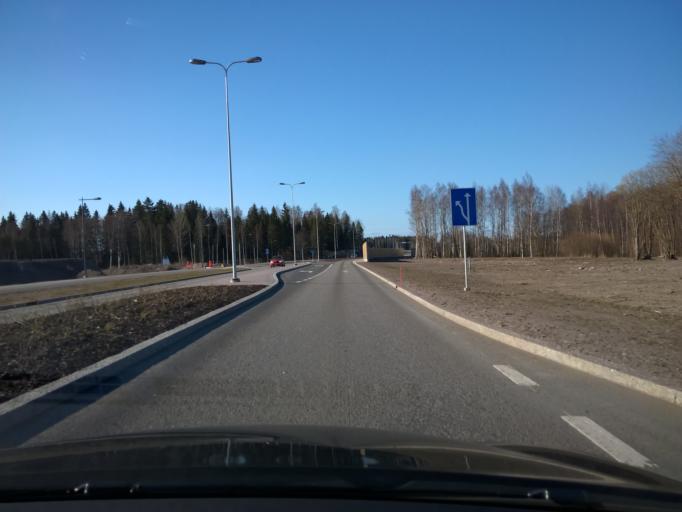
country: FI
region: Uusimaa
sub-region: Helsinki
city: Kilo
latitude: 60.2027
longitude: 24.7870
